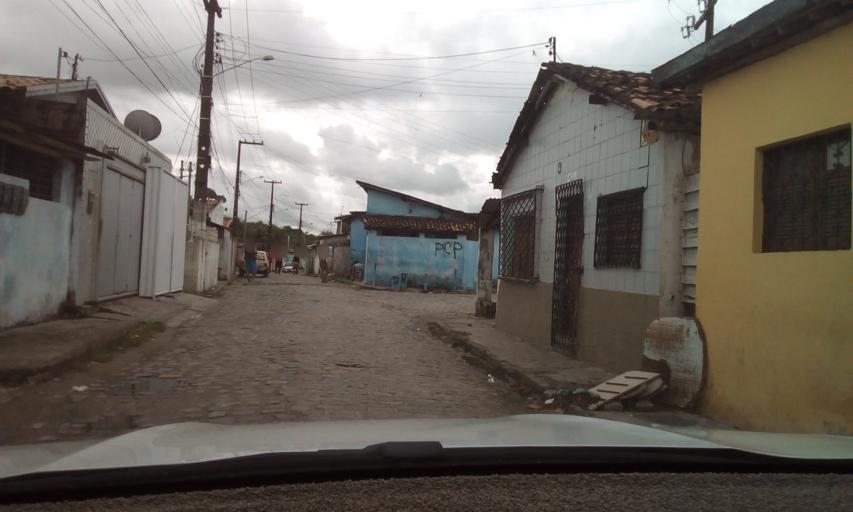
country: BR
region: Paraiba
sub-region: Joao Pessoa
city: Joao Pessoa
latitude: -7.1279
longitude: -34.8905
